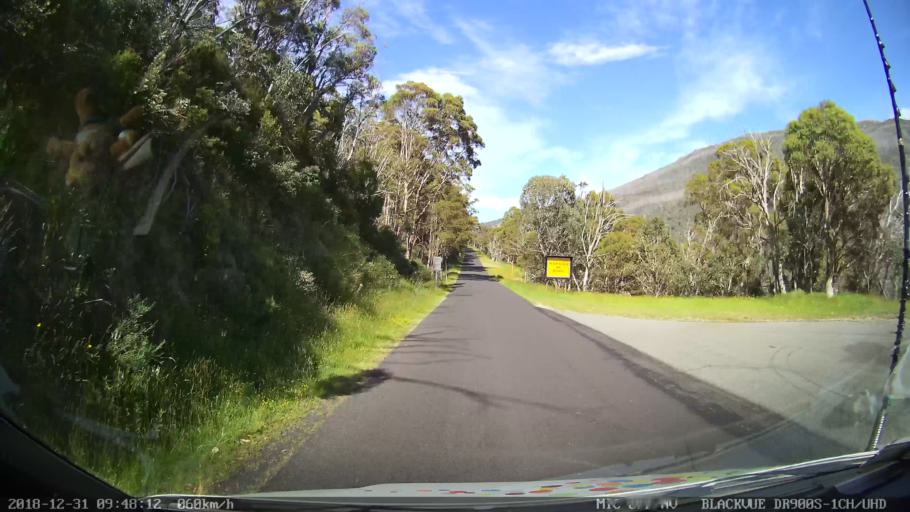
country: AU
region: New South Wales
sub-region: Snowy River
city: Jindabyne
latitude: -36.5118
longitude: 148.2950
